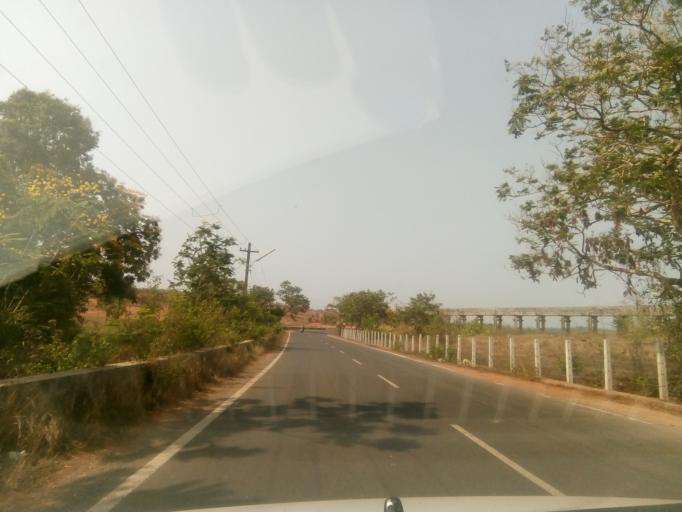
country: IN
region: Goa
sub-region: North Goa
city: Colovale
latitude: 15.6853
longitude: 73.8376
